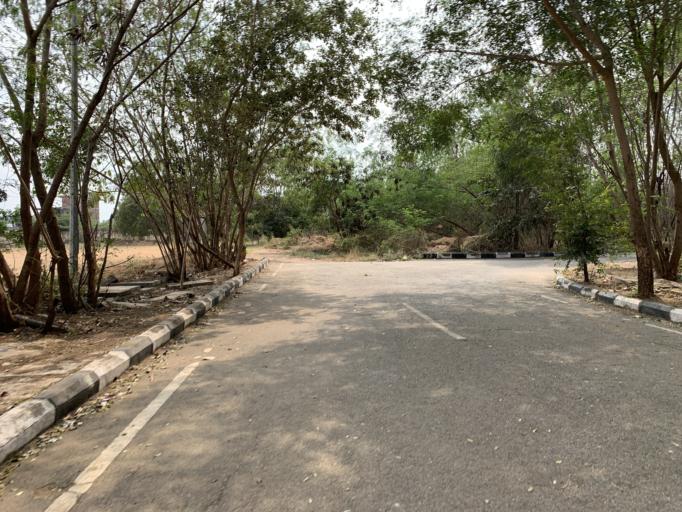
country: IN
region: Telangana
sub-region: Warangal
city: Warangal
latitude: 17.9823
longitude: 79.5352
